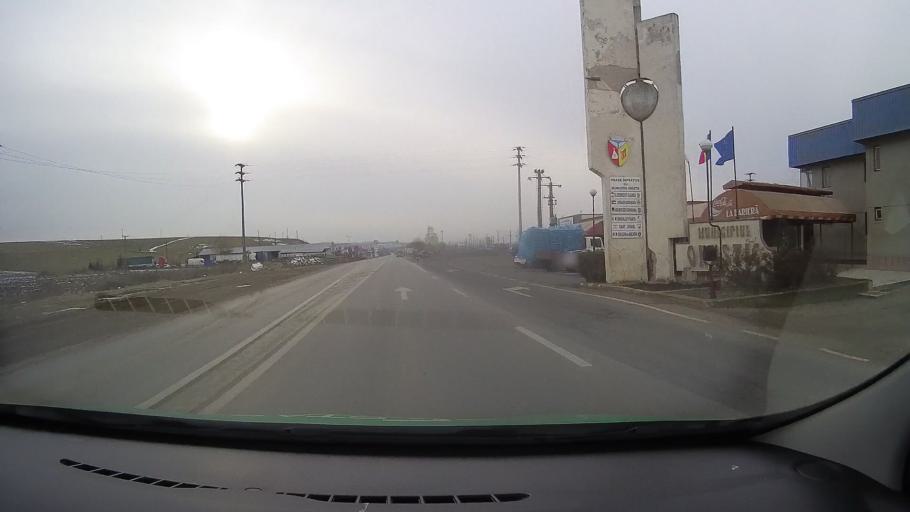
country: RO
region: Hunedoara
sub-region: Municipiul Orastie
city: Orastie
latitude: 45.8648
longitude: 23.2213
